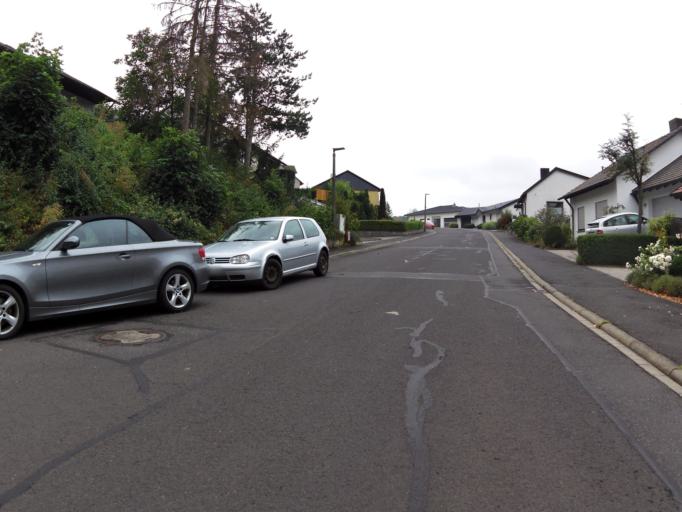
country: DE
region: Bavaria
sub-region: Regierungsbezirk Unterfranken
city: Guntersleben
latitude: 49.8641
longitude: 9.9059
